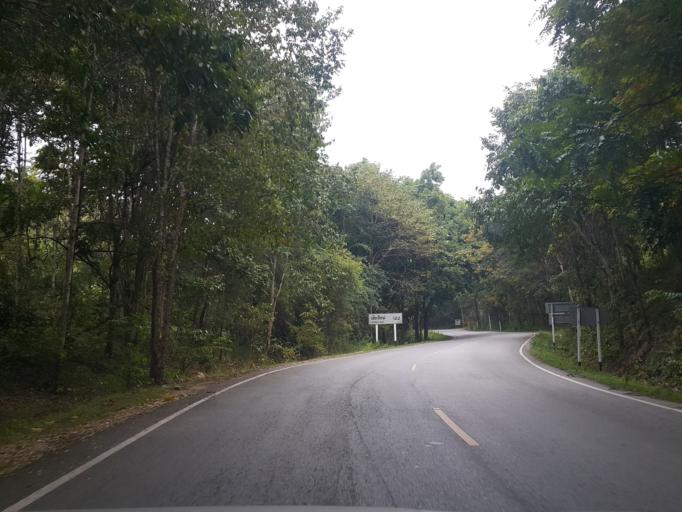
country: TH
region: Mae Hong Son
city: Mae Hi
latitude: 19.2844
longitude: 98.4851
